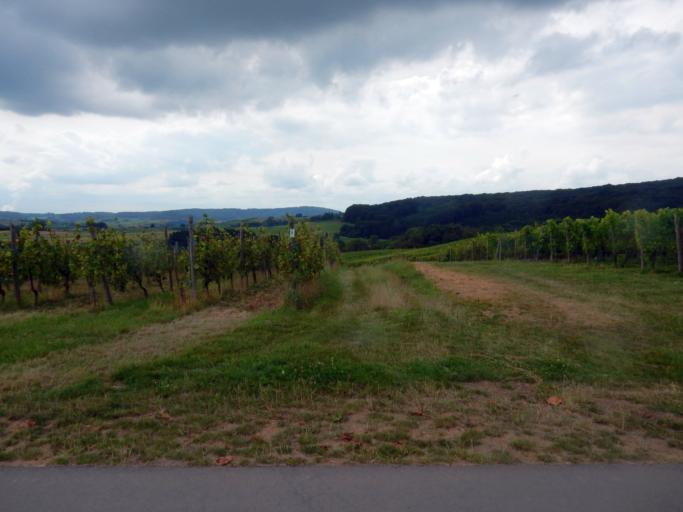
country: LU
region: Grevenmacher
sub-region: Canton de Remich
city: Stadtbredimus
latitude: 49.5706
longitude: 6.3513
